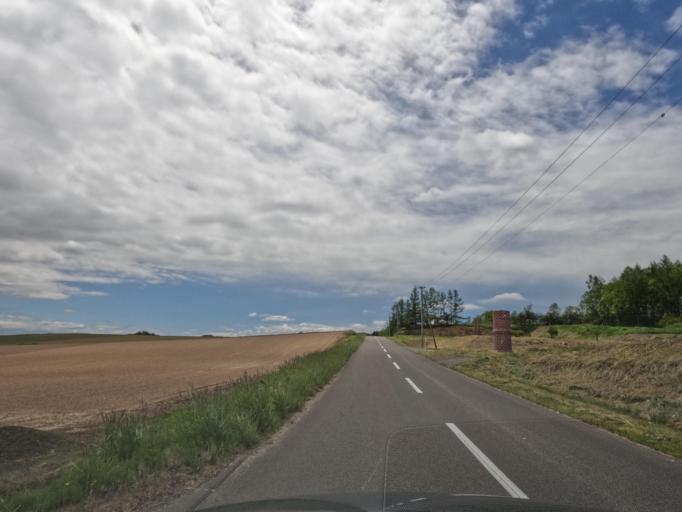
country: JP
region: Hokkaido
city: Shimo-furano
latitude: 43.5041
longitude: 142.4161
